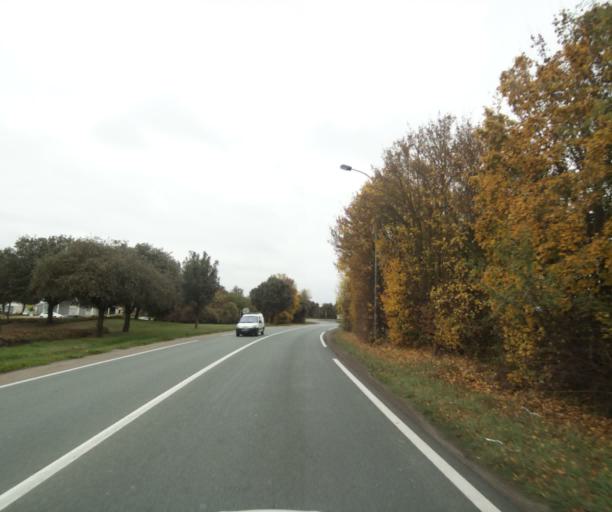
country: FR
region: Poitou-Charentes
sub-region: Departement de la Charente-Maritime
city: Les Gonds
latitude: 45.7227
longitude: -0.6390
